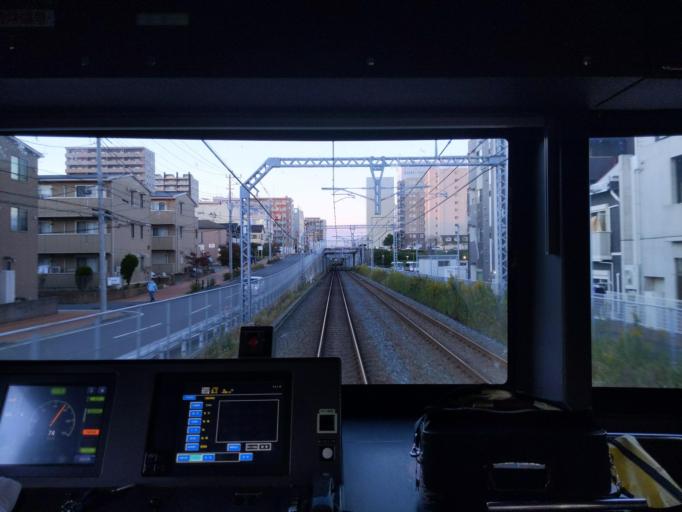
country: JP
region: Chiba
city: Shiroi
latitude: 35.7756
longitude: 139.9996
